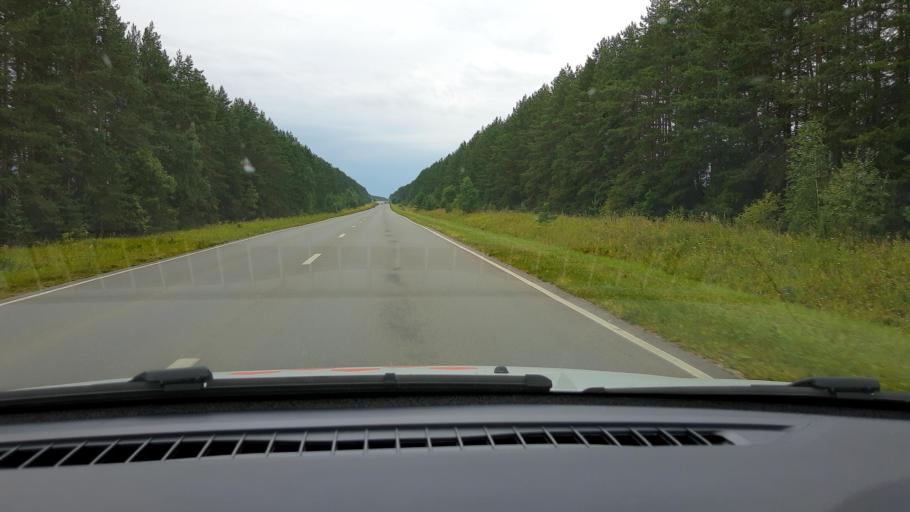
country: RU
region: Nizjnij Novgorod
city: Vyyezdnoye
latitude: 55.1823
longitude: 43.6068
